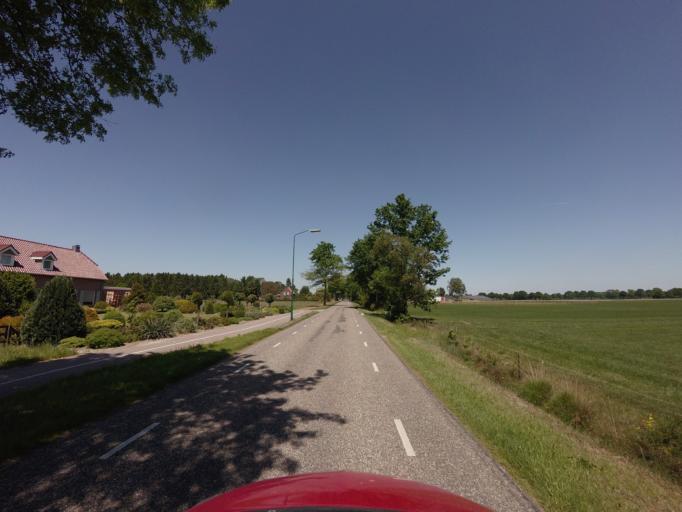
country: BE
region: Flanders
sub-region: Provincie Limburg
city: Lommel
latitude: 51.2707
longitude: 5.3161
